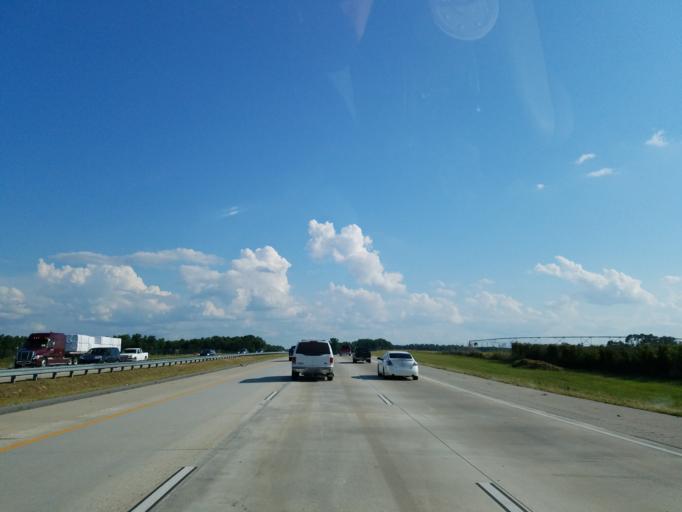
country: US
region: Georgia
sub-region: Dooly County
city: Unadilla
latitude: 32.1723
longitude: -83.7524
